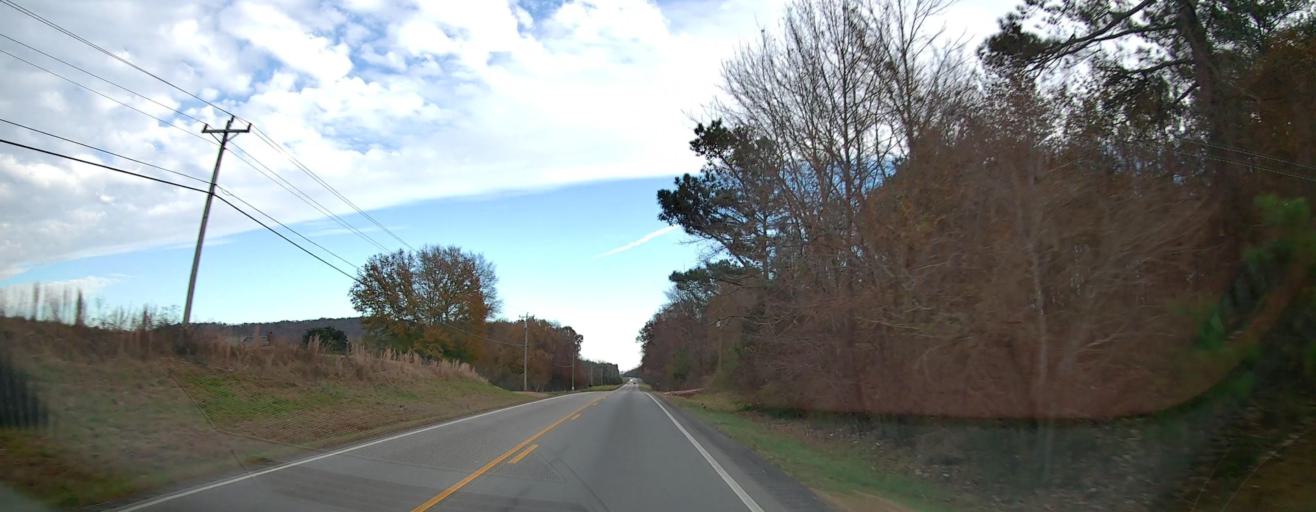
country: US
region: Alabama
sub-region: Morgan County
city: Priceville
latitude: 34.4435
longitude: -86.7521
